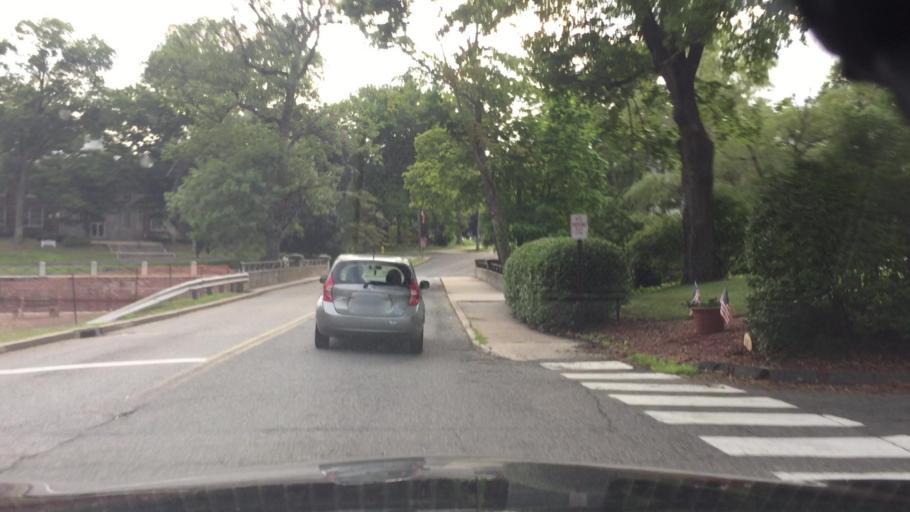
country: US
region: Connecticut
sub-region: New Haven County
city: Milford
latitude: 41.2265
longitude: -73.0576
